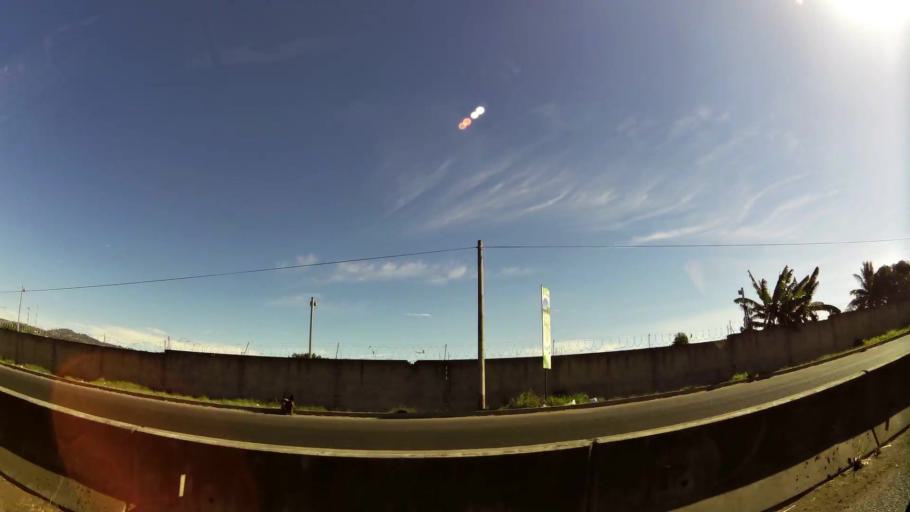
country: SV
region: Santa Ana
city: Santa Ana
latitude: 13.9725
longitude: -89.5848
